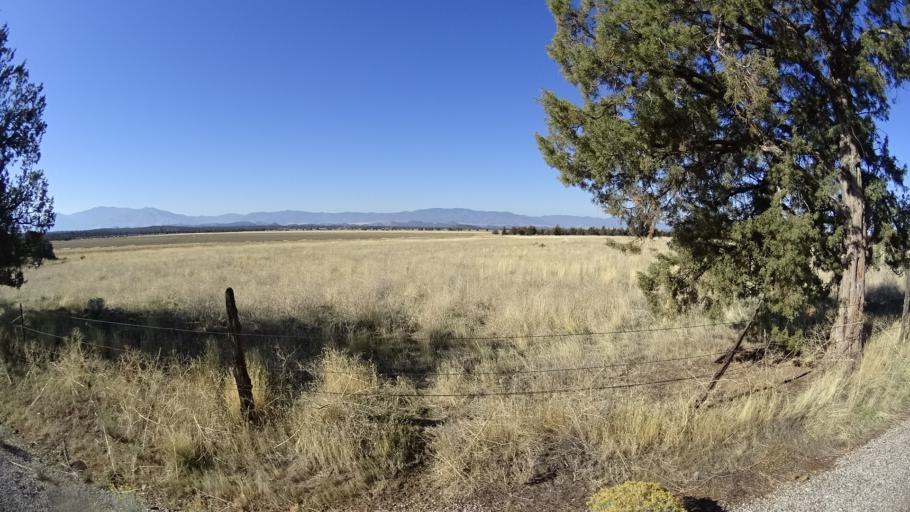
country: US
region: California
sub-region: Siskiyou County
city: Weed
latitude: 41.6005
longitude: -122.3019
